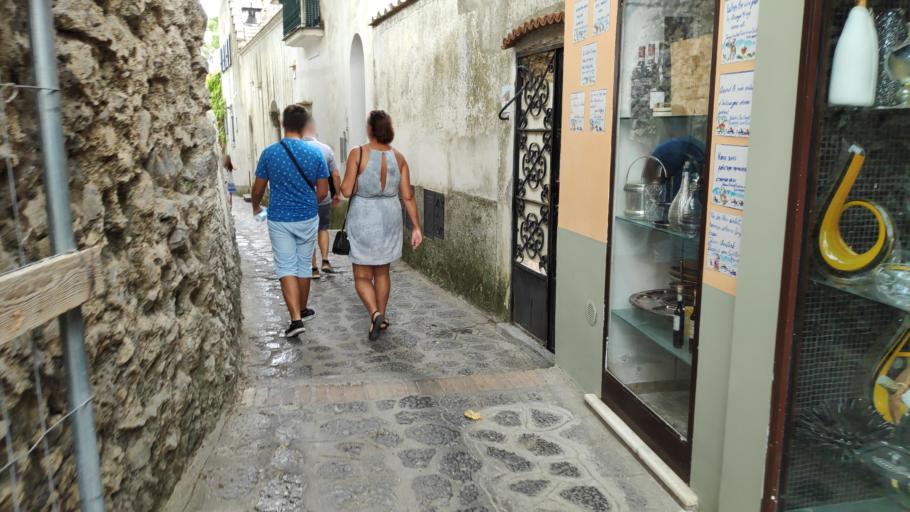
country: IT
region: Campania
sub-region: Provincia di Salerno
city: Ravello
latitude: 40.6464
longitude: 14.6105
